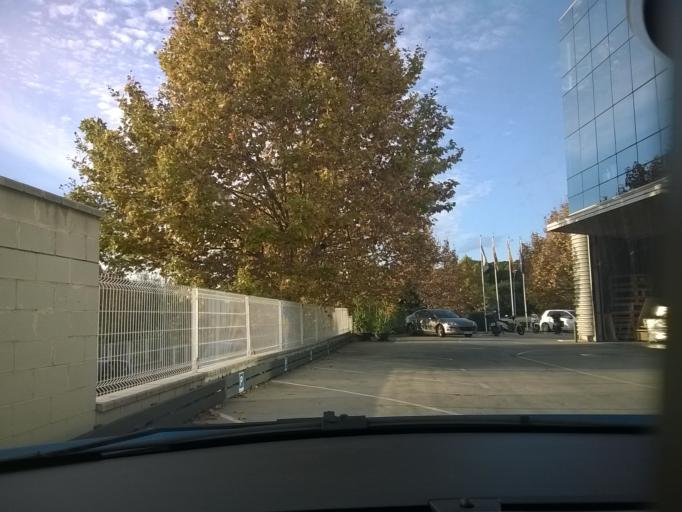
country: ES
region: Catalonia
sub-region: Provincia de Barcelona
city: Barbera del Valles
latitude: 41.5173
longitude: 2.1433
